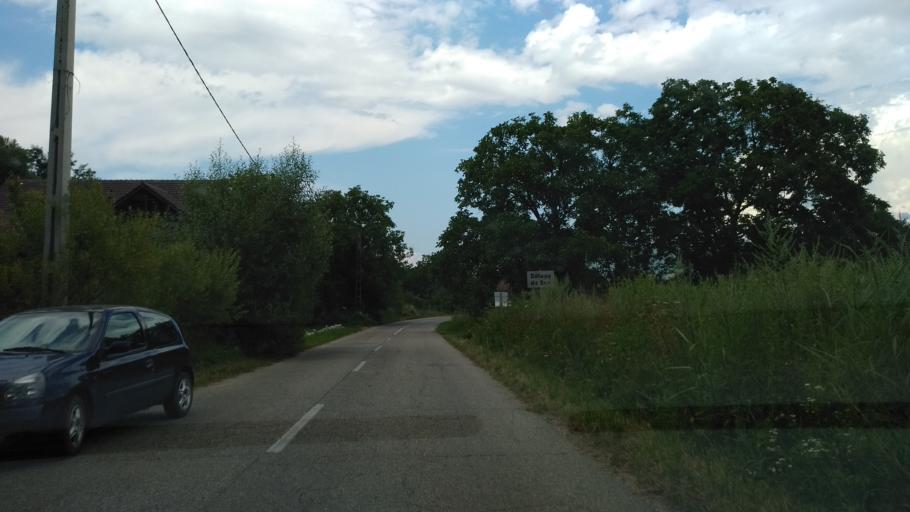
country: RO
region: Hunedoara
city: Salasu de Sus
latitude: 45.5050
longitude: 22.9506
